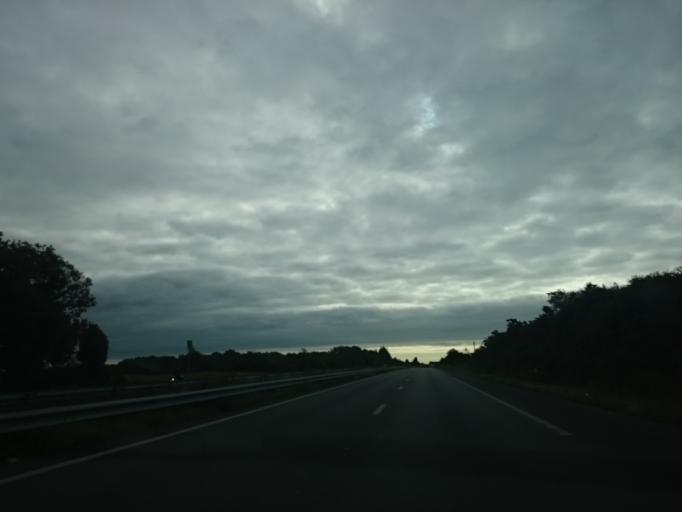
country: FR
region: Brittany
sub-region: Departement du Morbihan
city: Landaul
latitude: 47.7234
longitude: -3.0760
